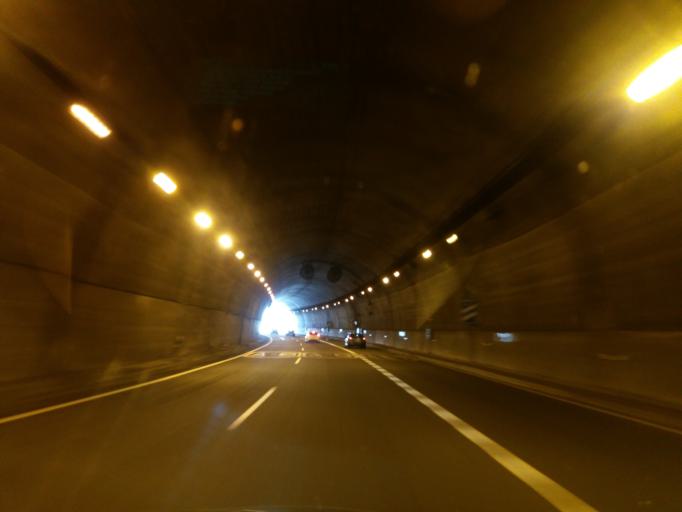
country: ES
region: Cantabria
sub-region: Provincia de Cantabria
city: Torrelavega
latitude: 43.3579
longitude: -4.0415
